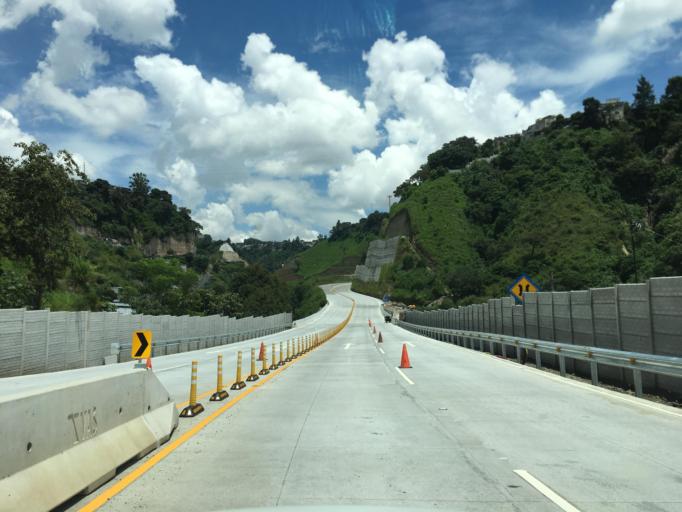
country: GT
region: Guatemala
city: Santa Catarina Pinula
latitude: 14.5515
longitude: -90.5325
